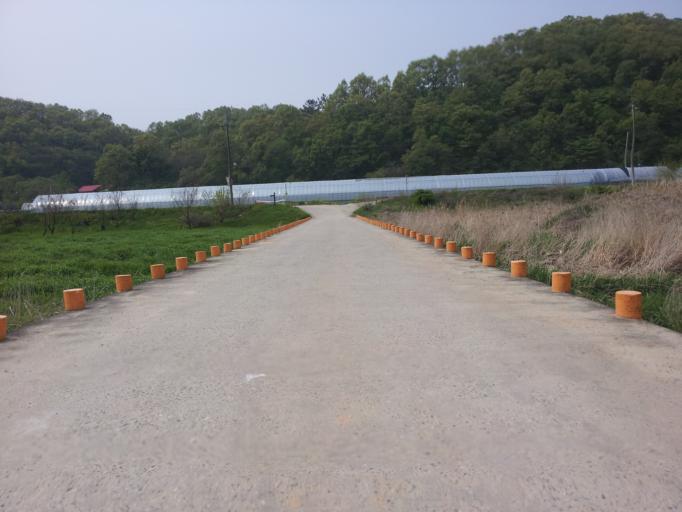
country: KR
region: Daejeon
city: Daejeon
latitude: 36.2711
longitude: 127.3398
